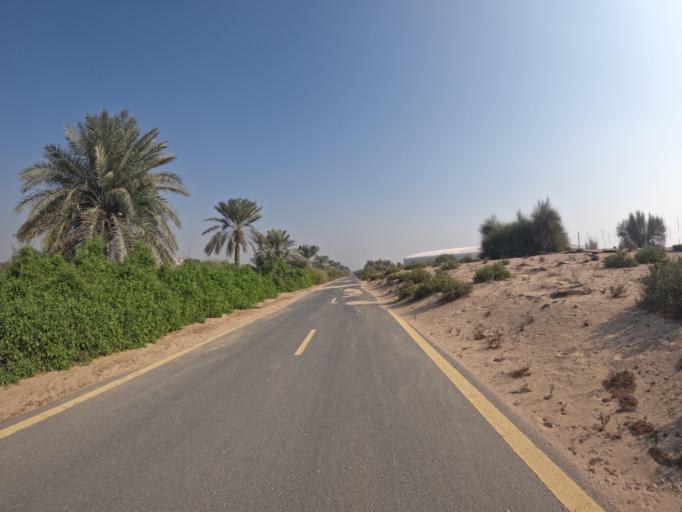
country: AE
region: Dubai
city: Dubai
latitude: 25.0797
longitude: 55.3116
